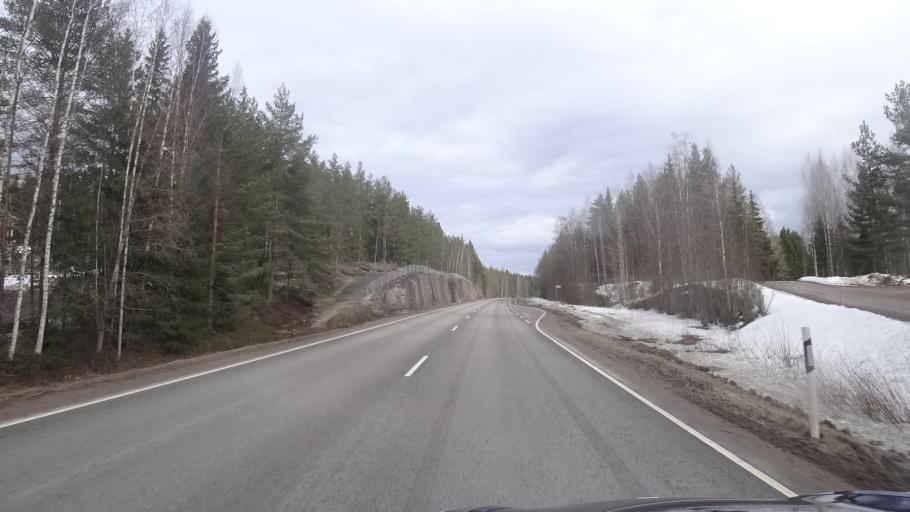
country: FI
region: Kymenlaakso
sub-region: Kouvola
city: Anjala
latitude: 60.6929
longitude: 26.7176
